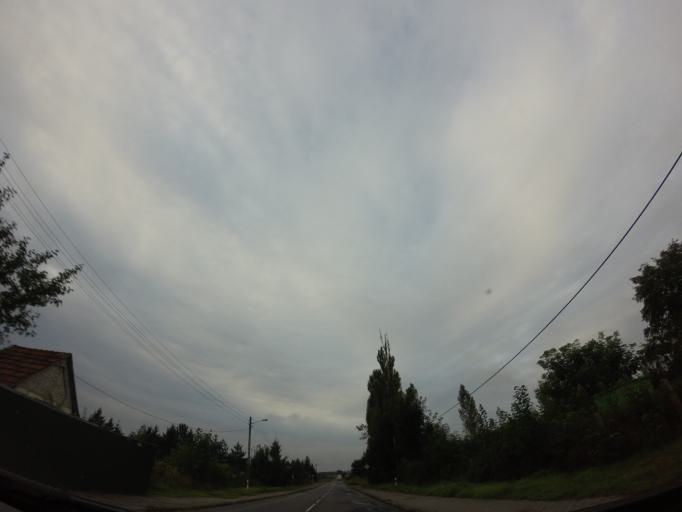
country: PL
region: Lubusz
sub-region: Powiat strzelecko-drezdenecki
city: Dobiegniew
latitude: 52.9627
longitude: 15.7509
